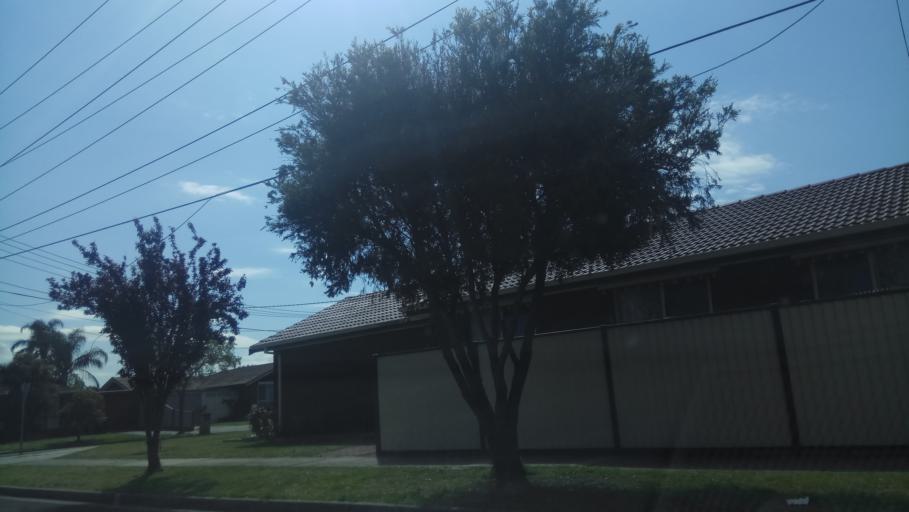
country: AU
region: Victoria
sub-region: Kingston
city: Clayton South
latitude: -37.9434
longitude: 145.1048
